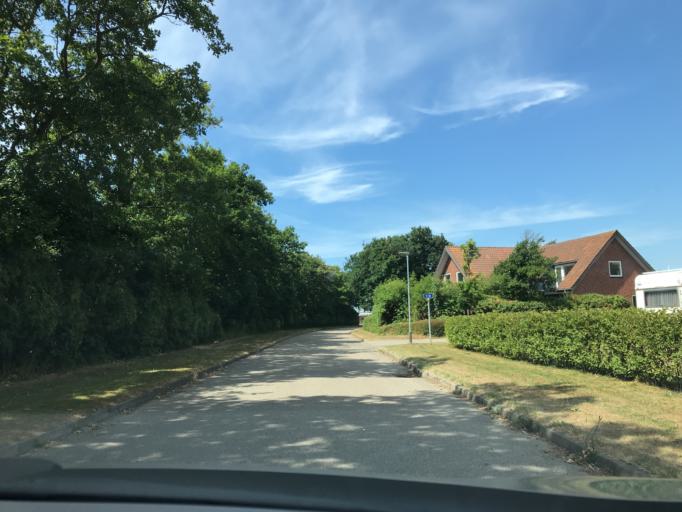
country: DK
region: Central Jutland
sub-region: Ringkobing-Skjern Kommune
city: Ringkobing
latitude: 56.0764
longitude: 8.2690
